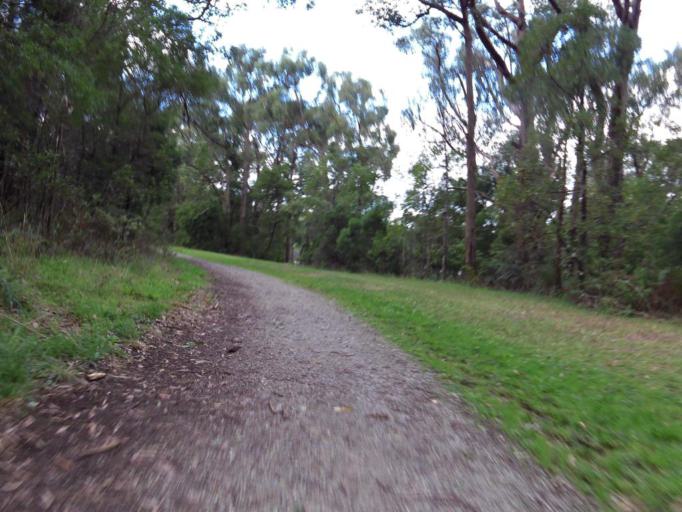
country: AU
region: Victoria
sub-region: Yarra Ranges
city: Mount Evelyn
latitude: -37.7898
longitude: 145.3817
